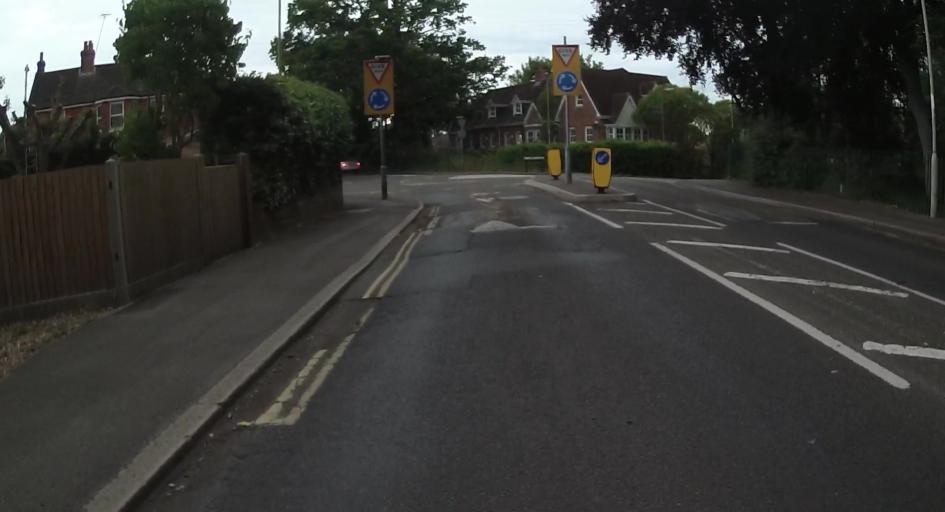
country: GB
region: England
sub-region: Hampshire
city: Aldershot
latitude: 51.2424
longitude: -0.7588
